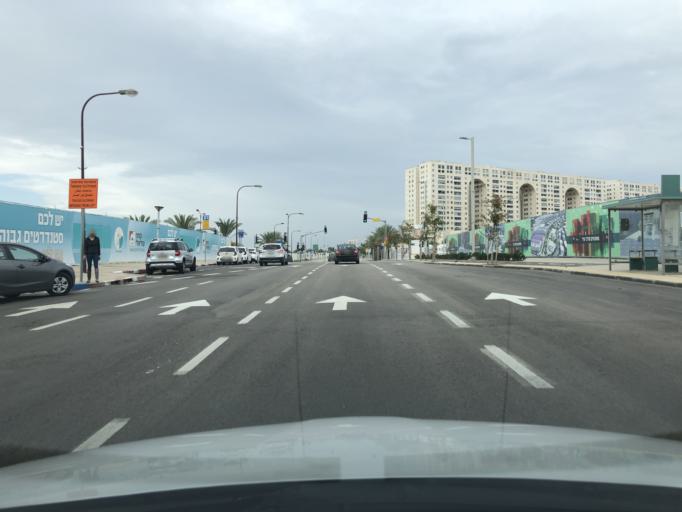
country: IL
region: Central District
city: Modiin
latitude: 31.9010
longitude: 35.0076
